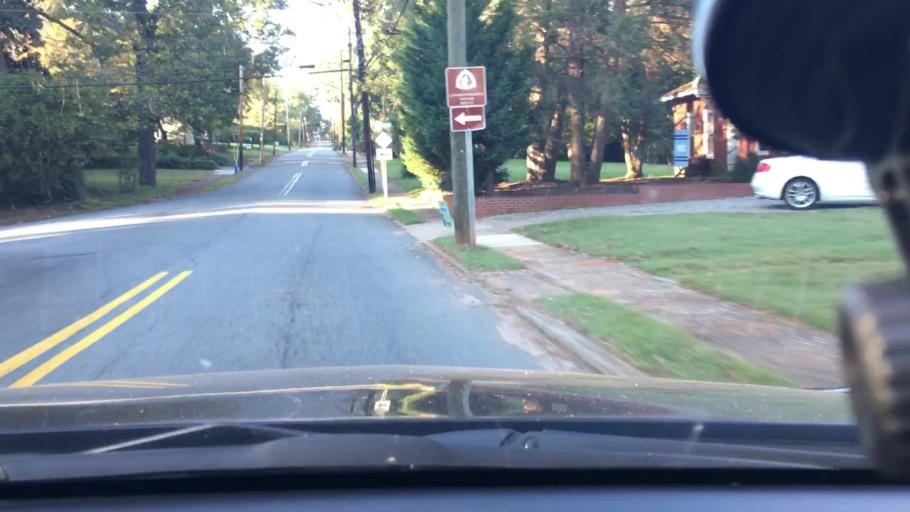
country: US
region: North Carolina
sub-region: Rutherford County
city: Rutherfordton
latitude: 35.3645
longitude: -81.9653
